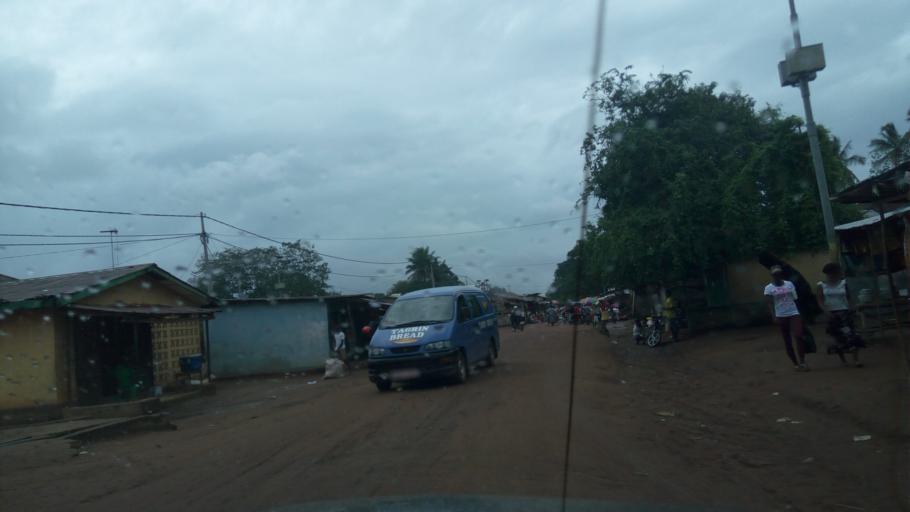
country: SL
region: Northern Province
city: Tintafor
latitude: 8.6288
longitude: -13.2176
